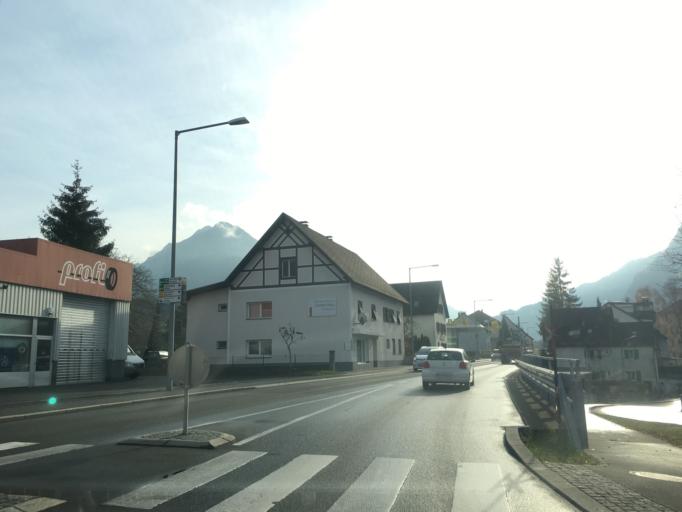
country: AT
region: Vorarlberg
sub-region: Politischer Bezirk Bludenz
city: Bludenz
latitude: 47.1509
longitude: 9.8251
